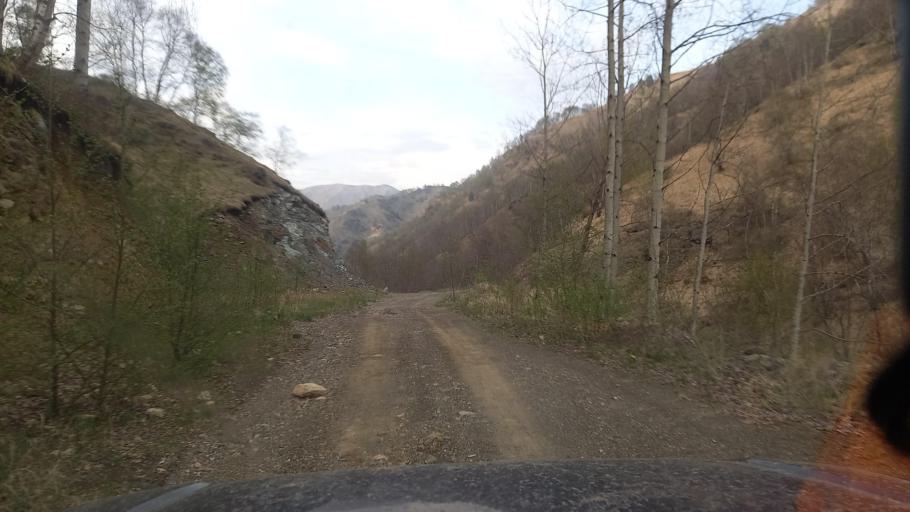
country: RU
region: Kabardino-Balkariya
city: Kamennomostskoye
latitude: 43.6999
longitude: 42.8427
